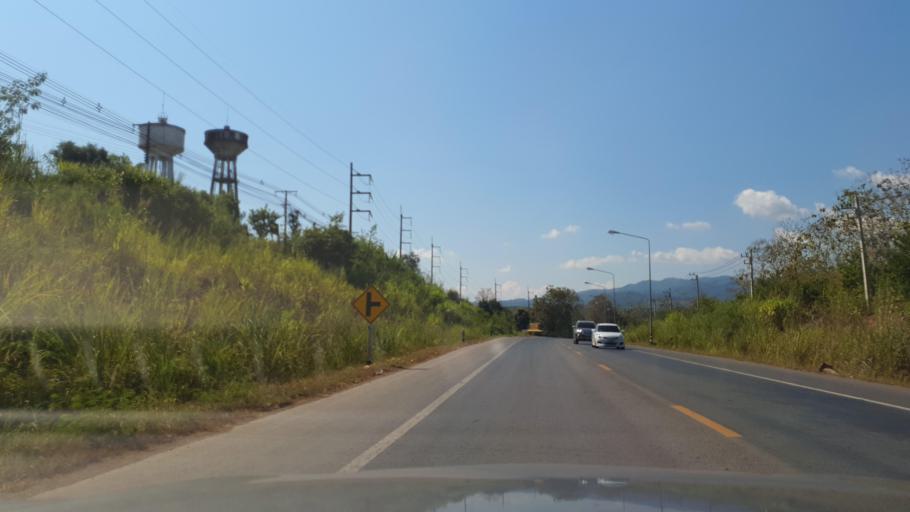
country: TH
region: Nan
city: Tha Wang Pha
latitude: 19.0170
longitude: 100.7850
